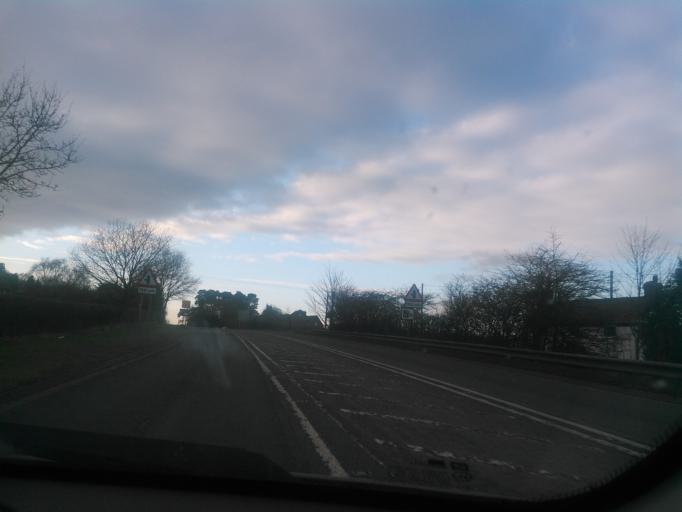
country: GB
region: England
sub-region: Shropshire
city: Market Drayton
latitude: 52.8405
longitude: -2.4636
